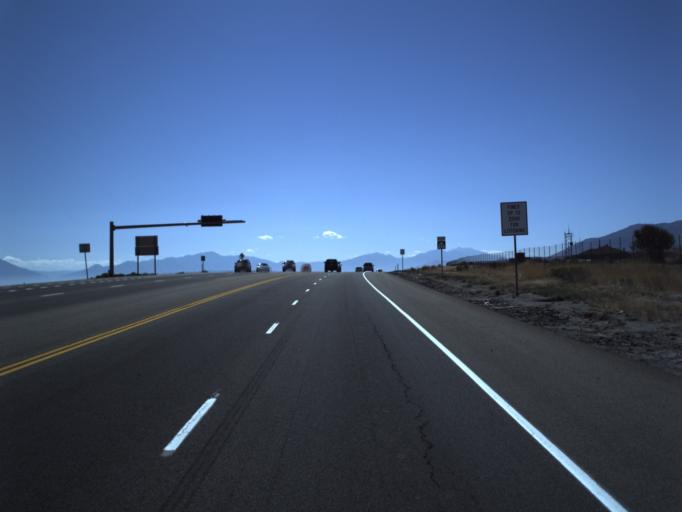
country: US
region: Utah
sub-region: Salt Lake County
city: Bluffdale
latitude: 40.4340
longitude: -111.9295
